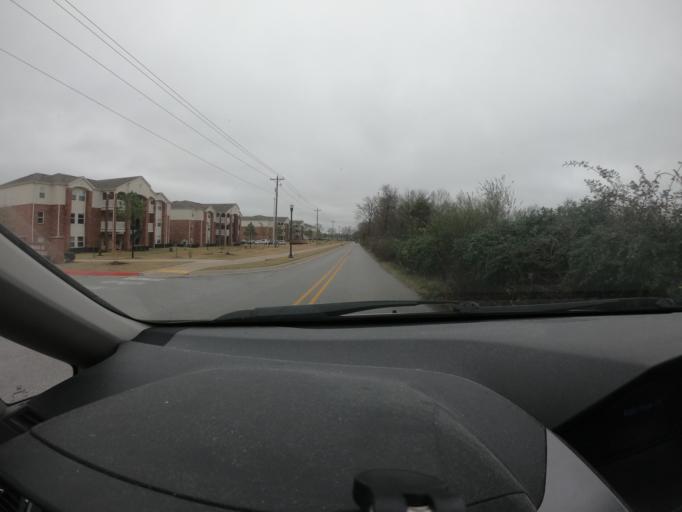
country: US
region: Arkansas
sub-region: Benton County
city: Bentonville
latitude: 36.3461
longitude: -94.2403
